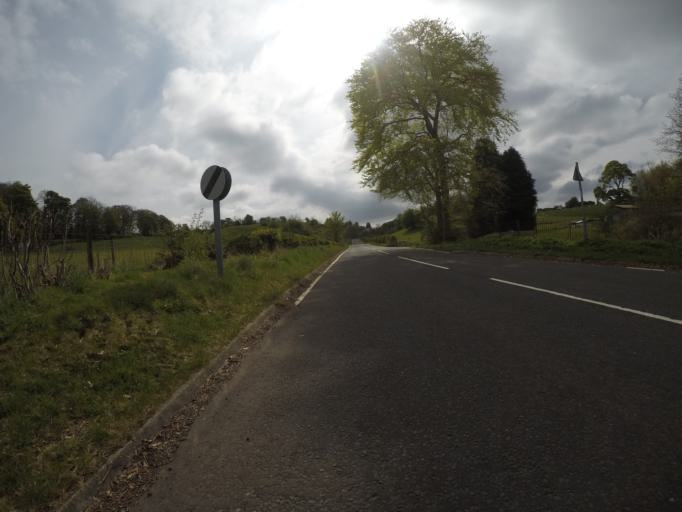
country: GB
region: Scotland
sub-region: East Renfrewshire
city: Newton Mearns
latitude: 55.7594
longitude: -4.3323
